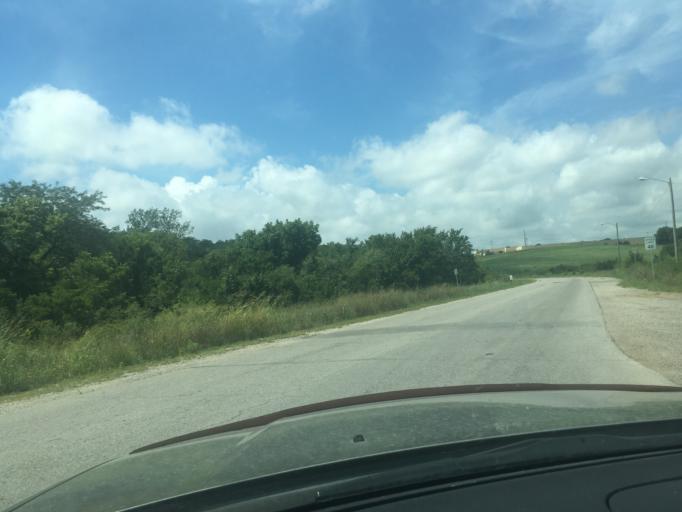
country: US
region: Kansas
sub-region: Atchison County
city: Atchison
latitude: 39.5381
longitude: -95.1221
